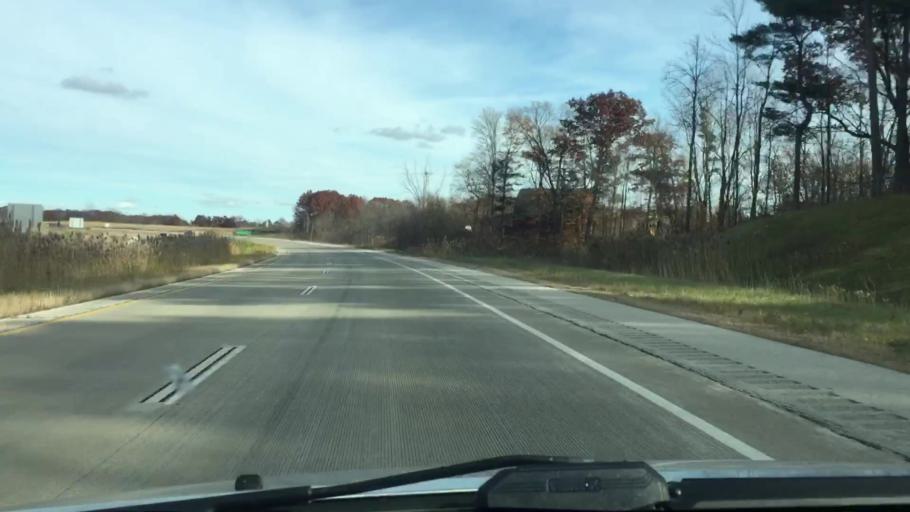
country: US
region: Wisconsin
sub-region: Kewaunee County
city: Luxemburg
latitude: 44.6337
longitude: -87.7645
